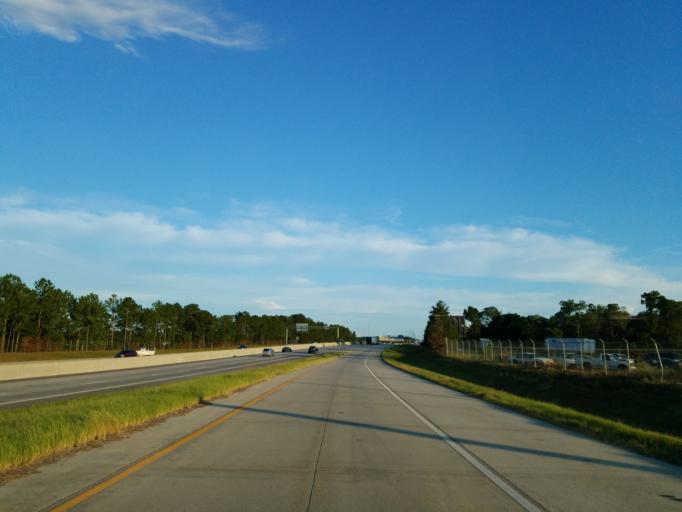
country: US
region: Georgia
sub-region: Cook County
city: Sparks
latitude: 31.2677
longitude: -83.4723
